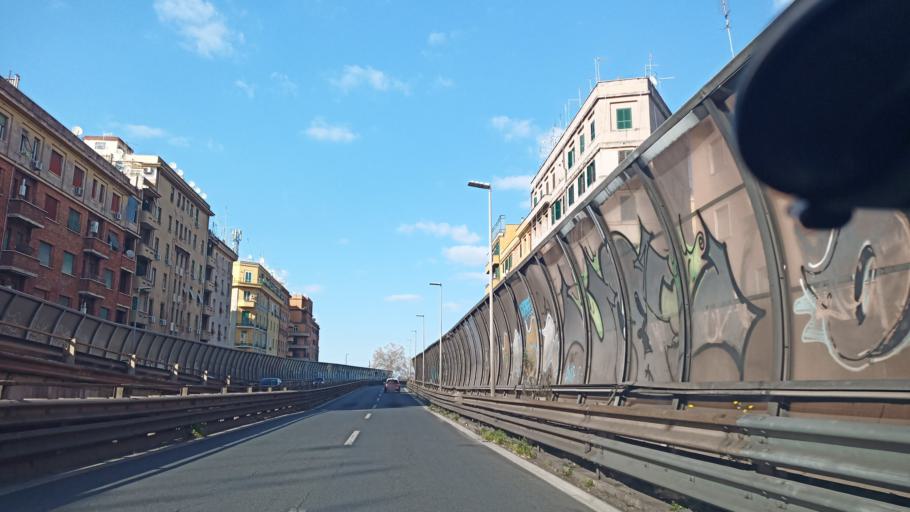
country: IT
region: Latium
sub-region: Citta metropolitana di Roma Capitale
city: Rome
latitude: 41.8956
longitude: 12.5180
